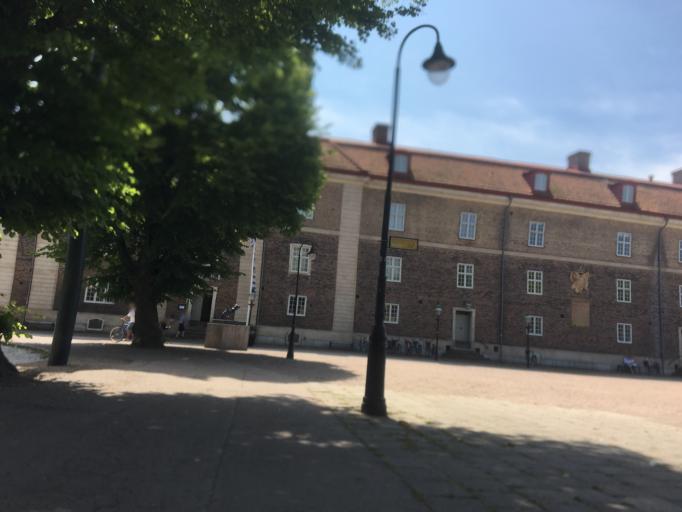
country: SE
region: Skane
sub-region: Landskrona
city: Landskrona
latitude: 55.8711
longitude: 12.8294
